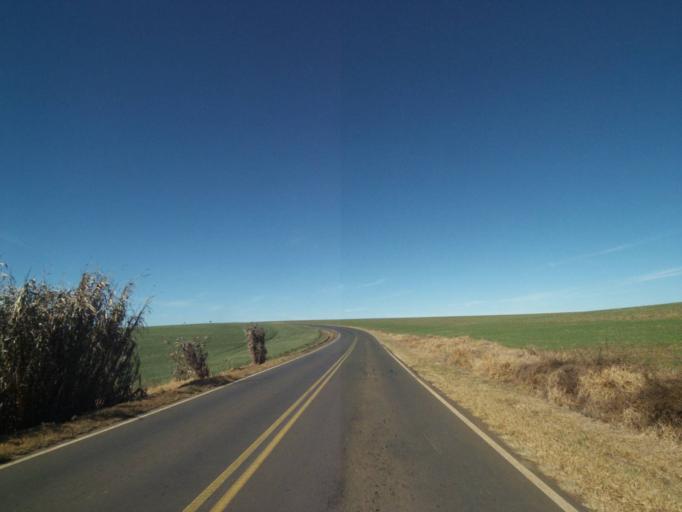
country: BR
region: Parana
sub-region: Tibagi
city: Tibagi
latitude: -24.5622
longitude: -50.2904
